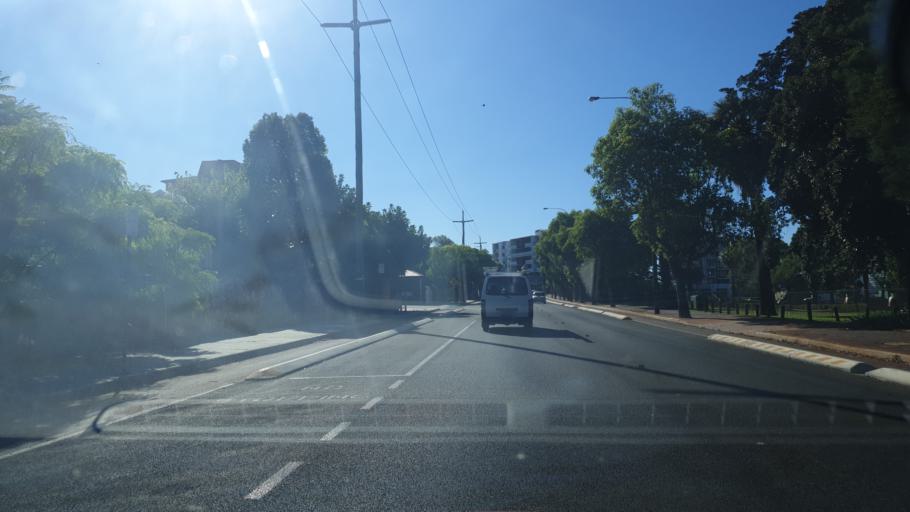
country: AU
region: Western Australia
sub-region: Vincent
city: Mount Lawley
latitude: -31.9442
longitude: 115.8705
